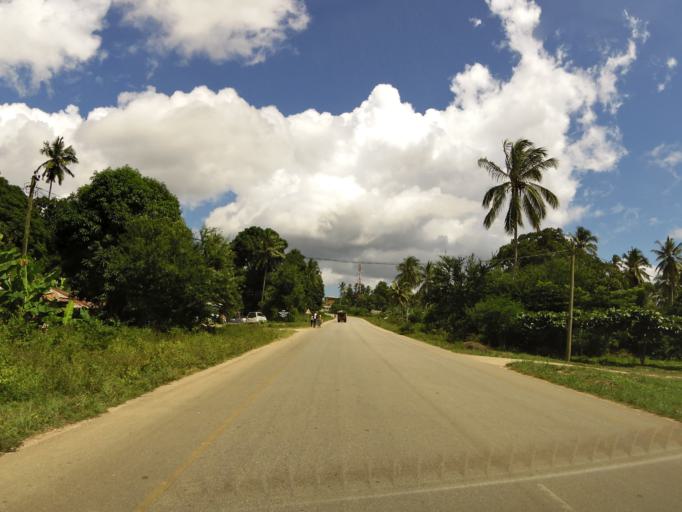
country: TZ
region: Zanzibar Central/South
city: Koani
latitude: -6.1357
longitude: 39.2914
